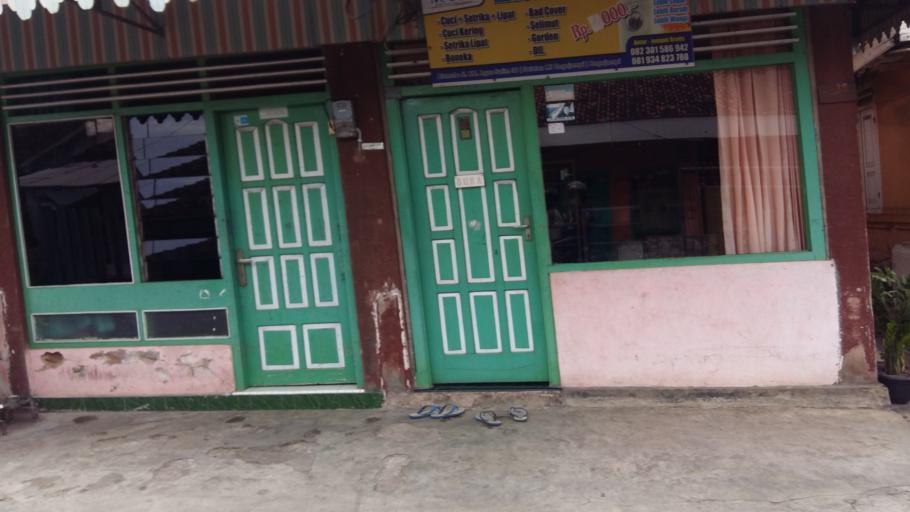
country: ID
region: East Java
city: Krajan
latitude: -8.3094
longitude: 114.2948
